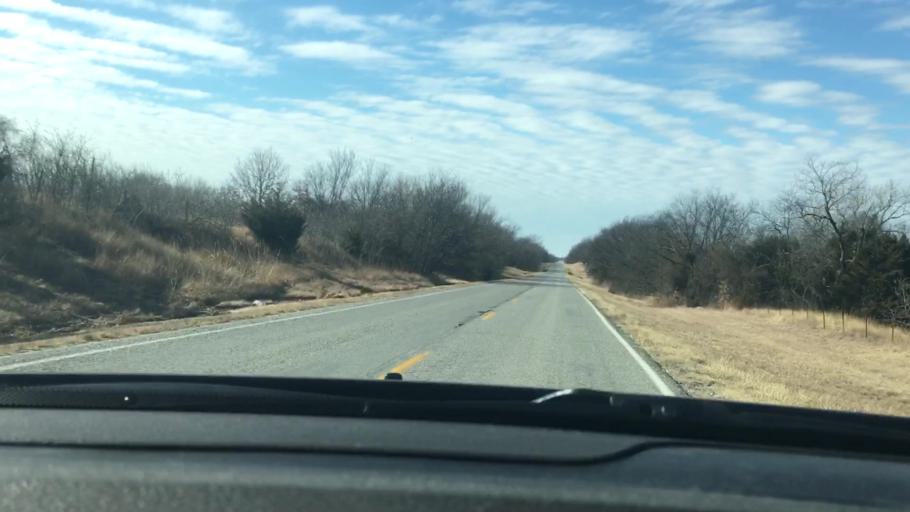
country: US
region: Oklahoma
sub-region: Garvin County
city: Wynnewood
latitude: 34.6515
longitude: -97.1143
